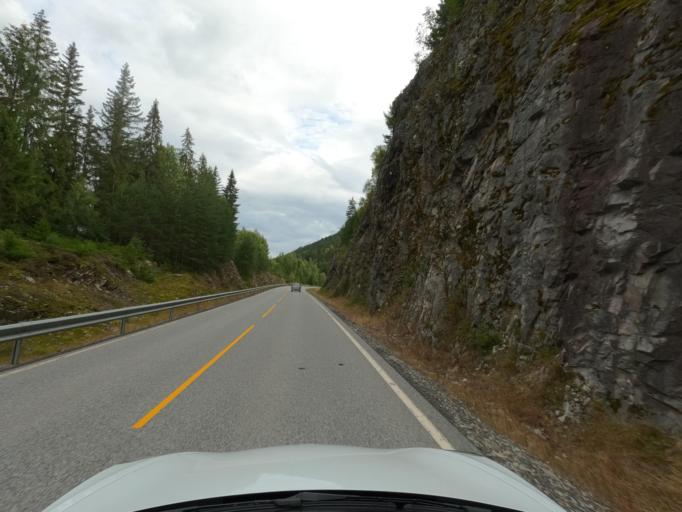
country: NO
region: Telemark
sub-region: Hjartdal
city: Sauland
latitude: 59.8105
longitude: 8.9903
